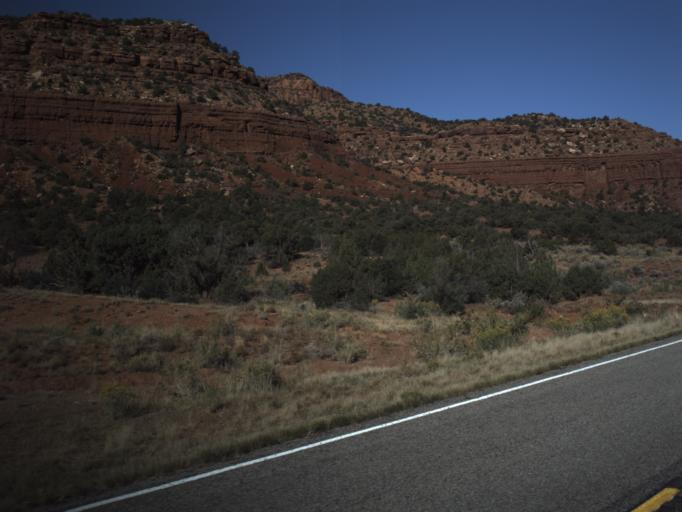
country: US
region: Utah
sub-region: San Juan County
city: Blanding
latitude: 37.6415
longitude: -110.1631
